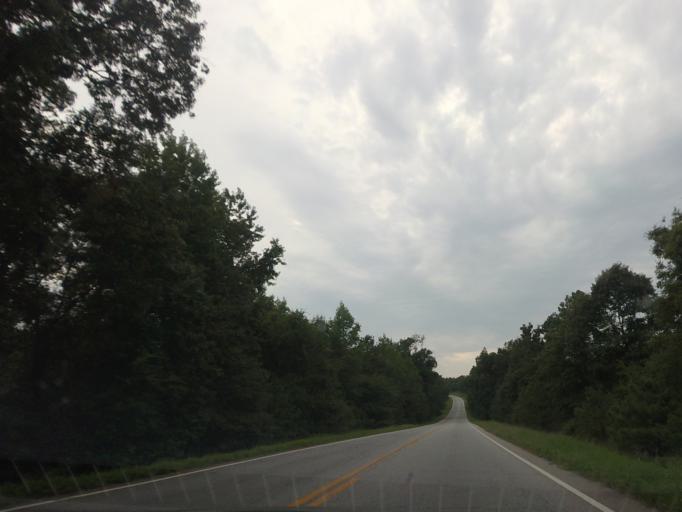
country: US
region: Georgia
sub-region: Twiggs County
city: Jeffersonville
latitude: 32.7622
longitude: -83.4593
